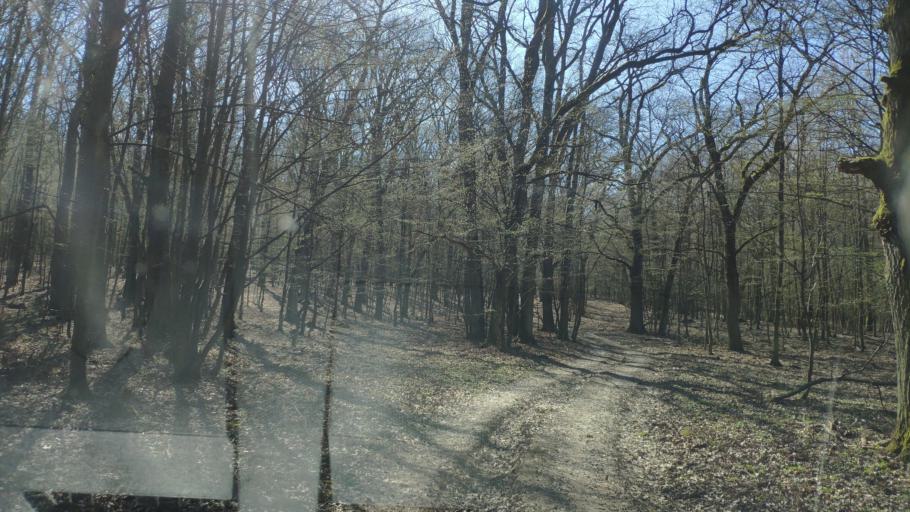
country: SK
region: Kosicky
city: Moldava nad Bodvou
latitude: 48.5659
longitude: 20.9347
